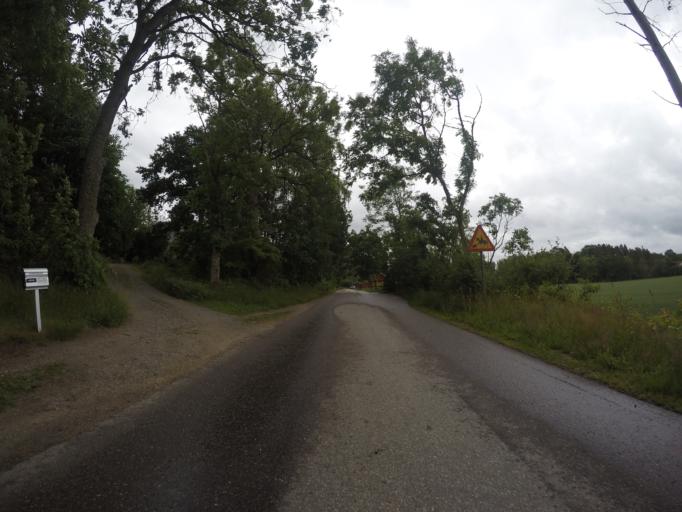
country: SE
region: Vaestra Goetaland
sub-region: Trollhattan
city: Sjuntorp
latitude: 58.1969
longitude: 12.2436
